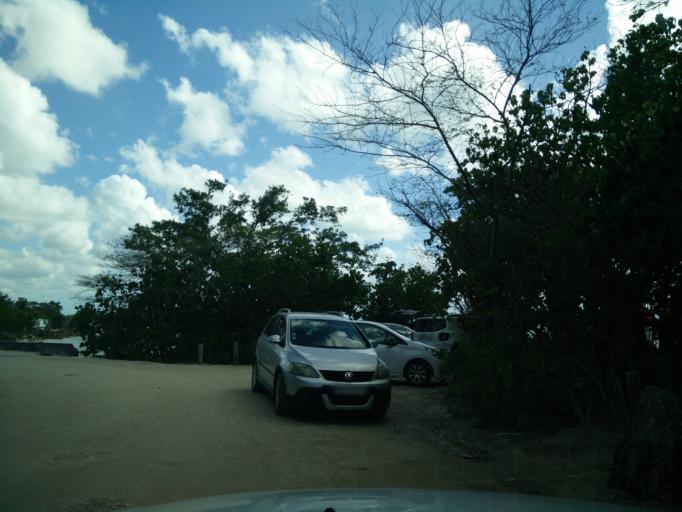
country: GP
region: Guadeloupe
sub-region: Guadeloupe
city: Port-Louis
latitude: 16.4312
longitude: -61.5370
